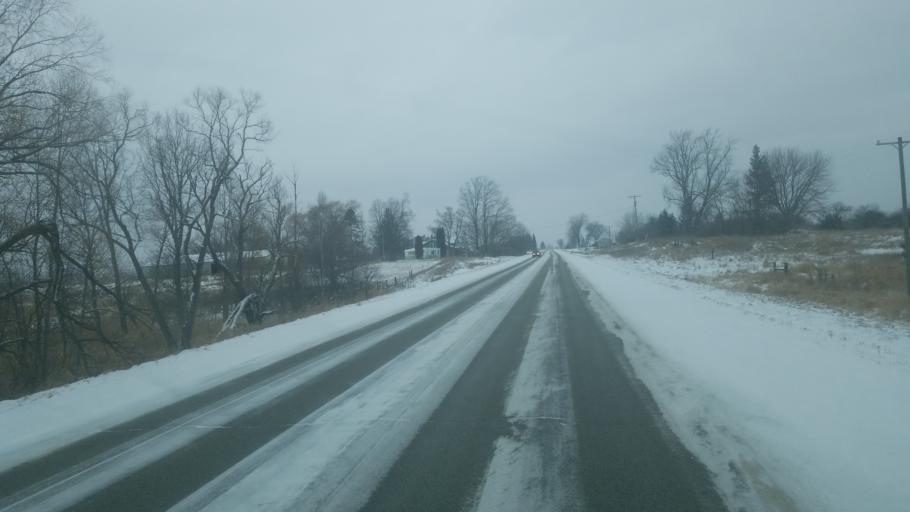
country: US
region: Michigan
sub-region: Osceola County
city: Evart
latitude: 43.9050
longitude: -85.1478
